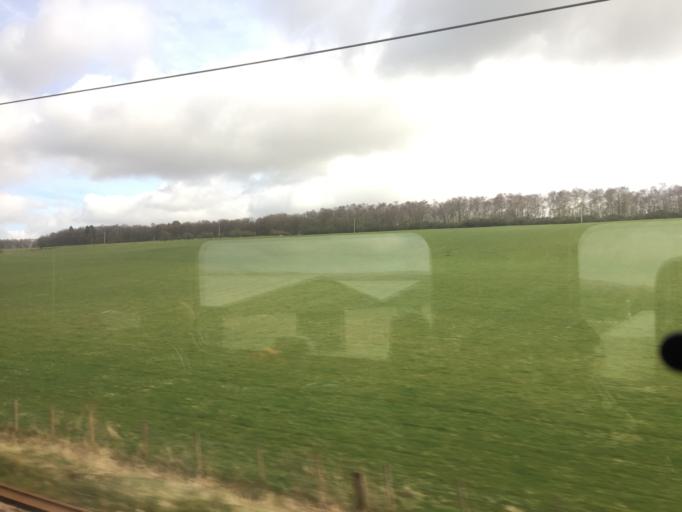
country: GB
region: Scotland
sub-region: Dumfries and Galloway
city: Lochmaben
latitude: 55.1886
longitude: -3.4038
